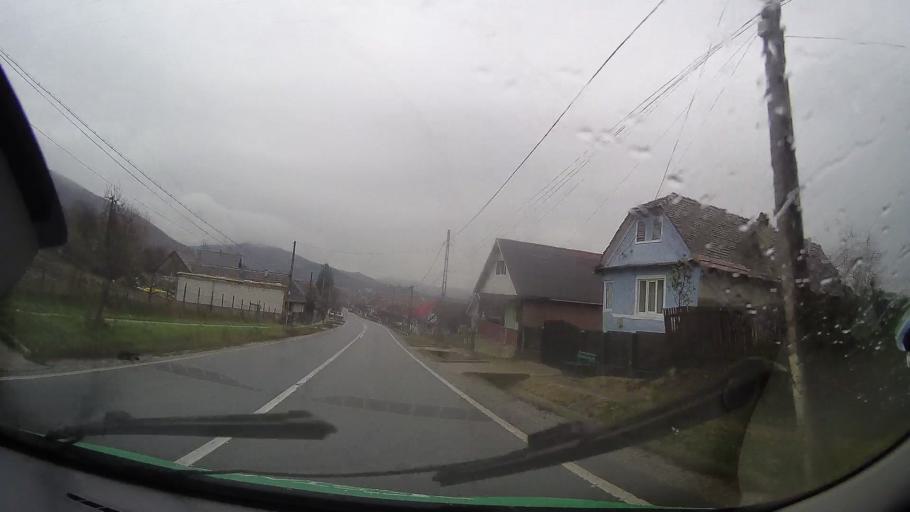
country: RO
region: Bistrita-Nasaud
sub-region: Comuna Galatii Bistritei
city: Galatii Bistritei
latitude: 46.9907
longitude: 24.4220
